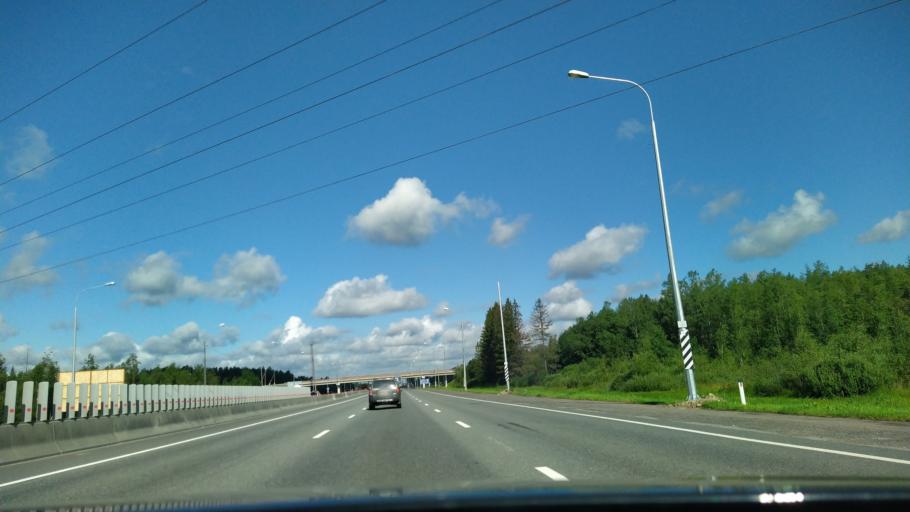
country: RU
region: Leningrad
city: Ul'yanovka
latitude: 59.6034
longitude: 30.7639
